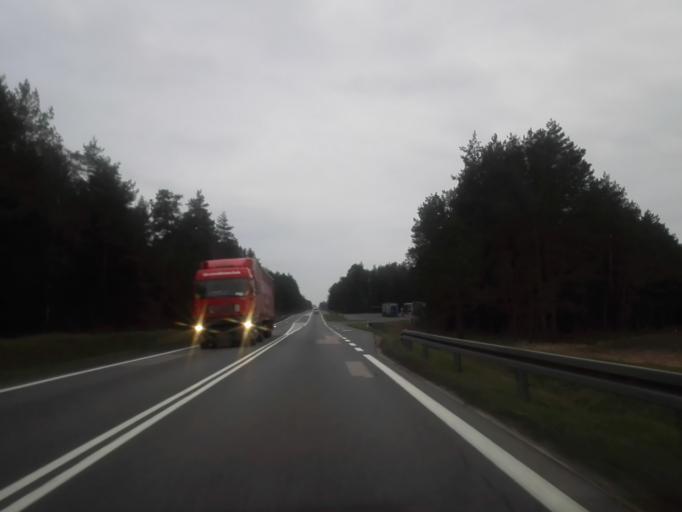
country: PL
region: Podlasie
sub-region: Powiat kolnenski
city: Stawiski
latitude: 53.4468
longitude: 22.1834
